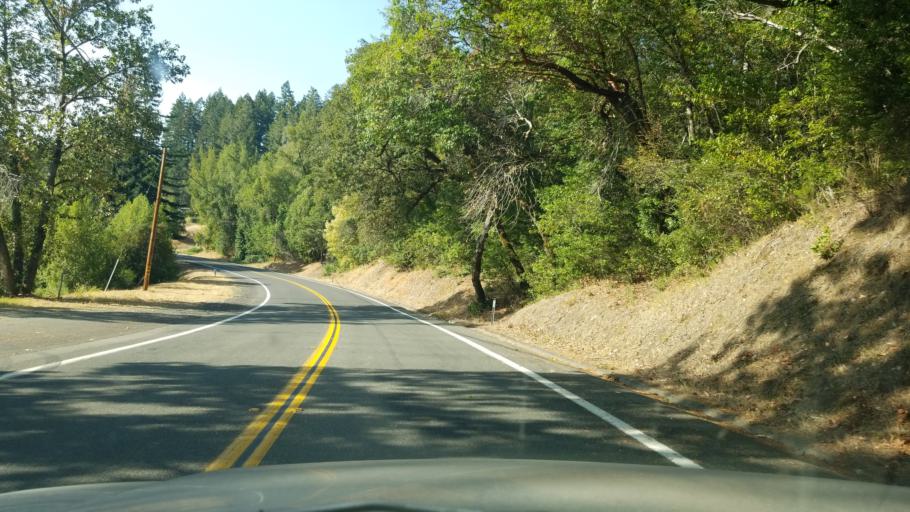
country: US
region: California
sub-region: Humboldt County
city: Redway
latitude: 40.1934
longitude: -123.7683
